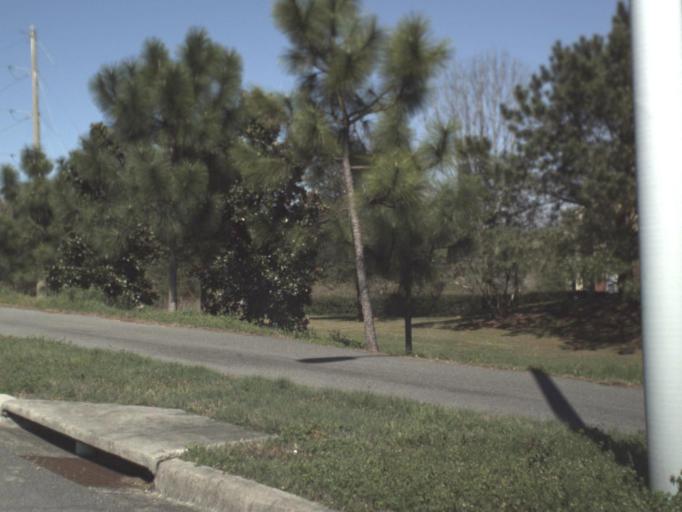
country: US
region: Florida
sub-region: Leon County
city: Tallahassee
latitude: 30.4043
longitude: -84.2348
